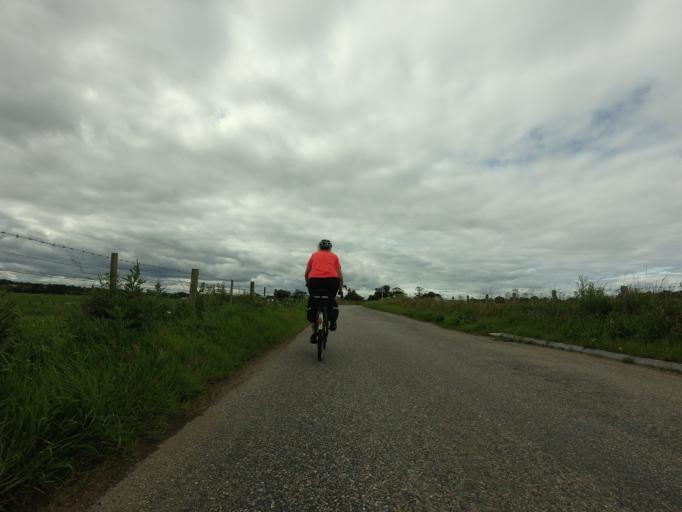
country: GB
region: Scotland
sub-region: Moray
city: Forres
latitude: 57.6234
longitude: -3.6097
